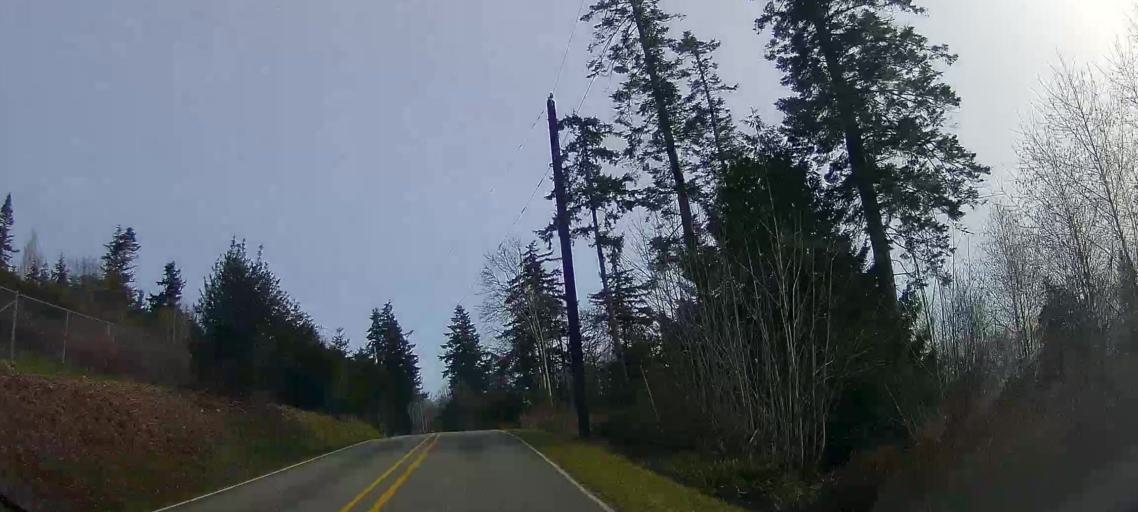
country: US
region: Washington
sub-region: Island County
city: Langley
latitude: 48.0581
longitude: -122.3693
